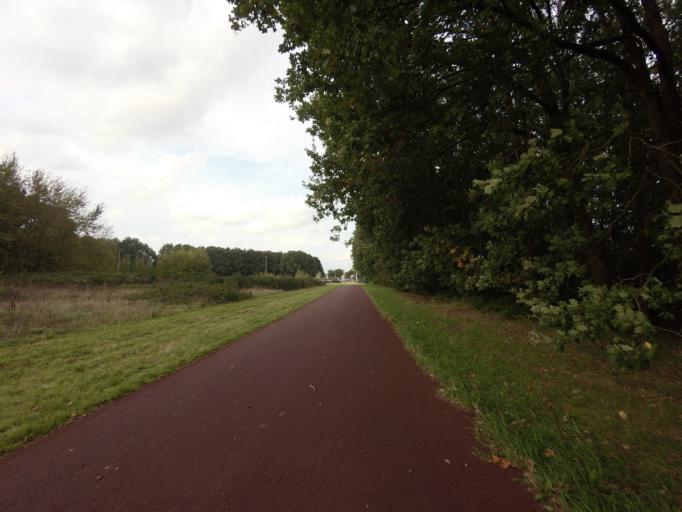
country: NL
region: North Brabant
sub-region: Gemeente Breda
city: Breda
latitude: 51.5657
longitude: 4.7429
